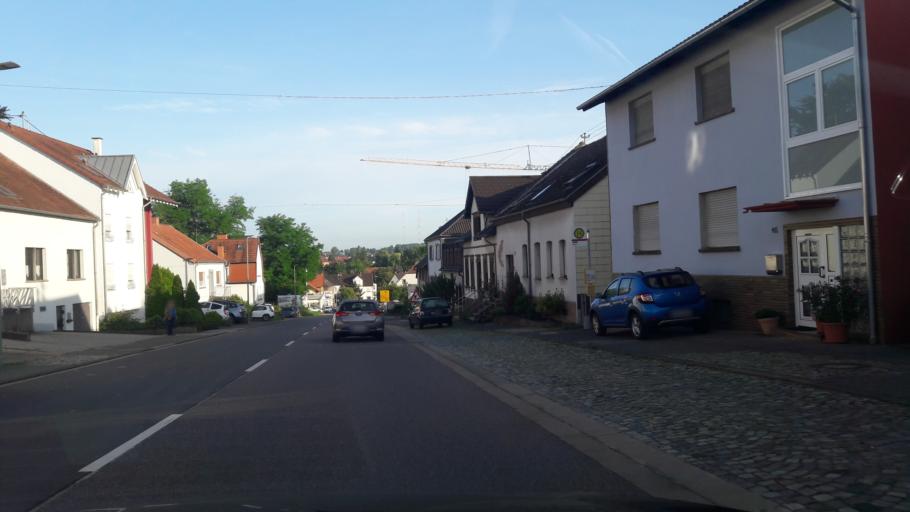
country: DE
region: Saarland
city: Heusweiler
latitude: 49.3279
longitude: 6.9346
